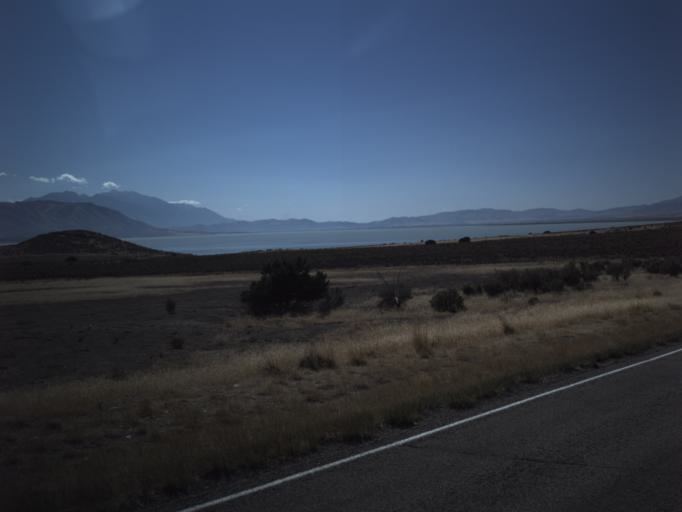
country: US
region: Utah
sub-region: Utah County
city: Saratoga Springs
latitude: 40.2013
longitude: -111.8995
